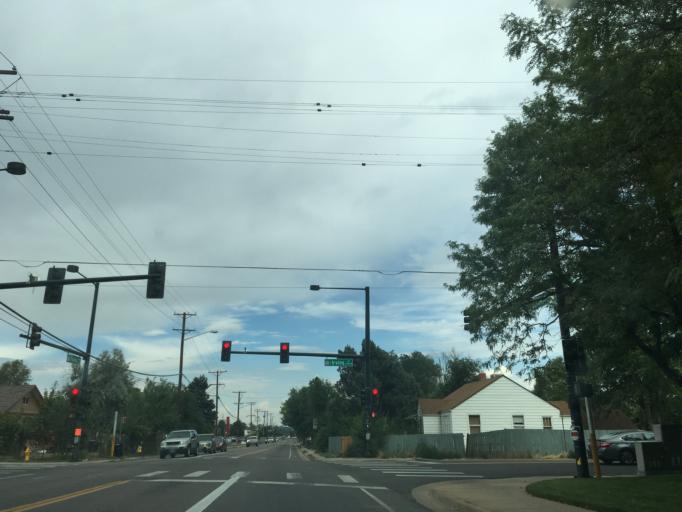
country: US
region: Colorado
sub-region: Arapahoe County
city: Sheridan
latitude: 39.6895
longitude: -105.0302
